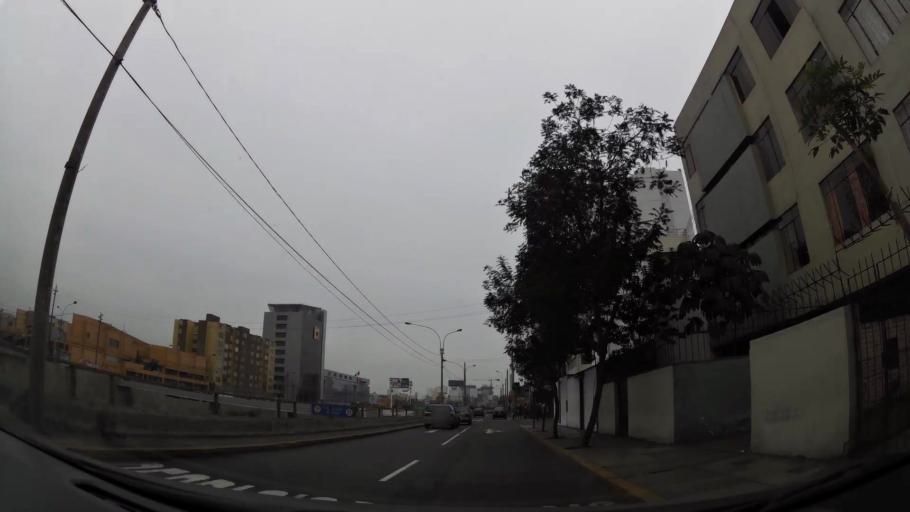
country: PE
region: Lima
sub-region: Lima
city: San Isidro
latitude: -12.1101
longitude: -77.0265
